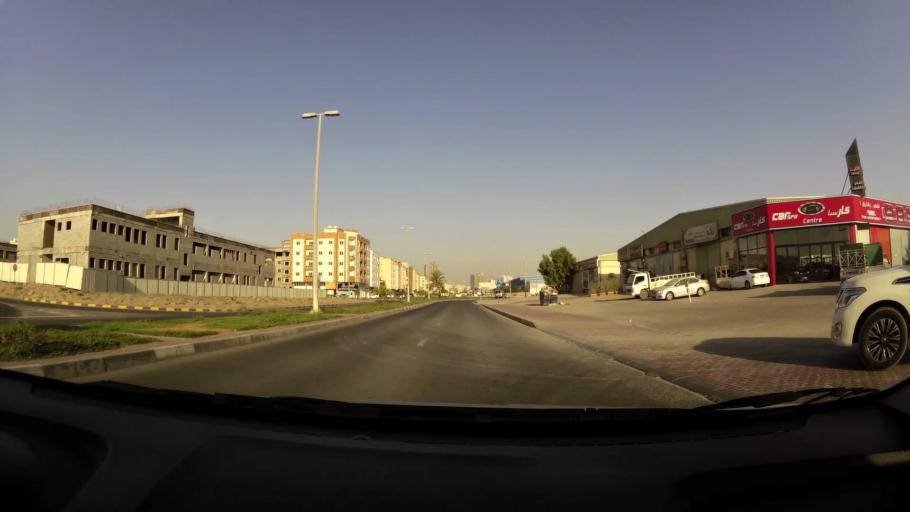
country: AE
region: Ajman
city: Ajman
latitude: 25.4035
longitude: 55.4978
